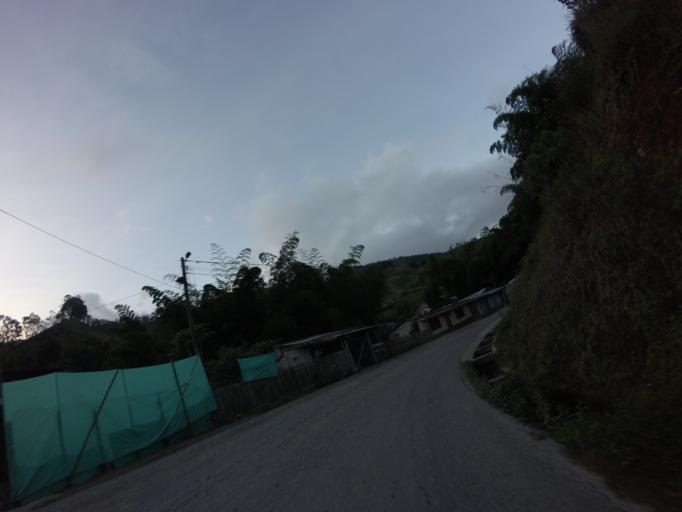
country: CO
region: Caldas
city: Manzanares
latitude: 5.2629
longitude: -75.1472
